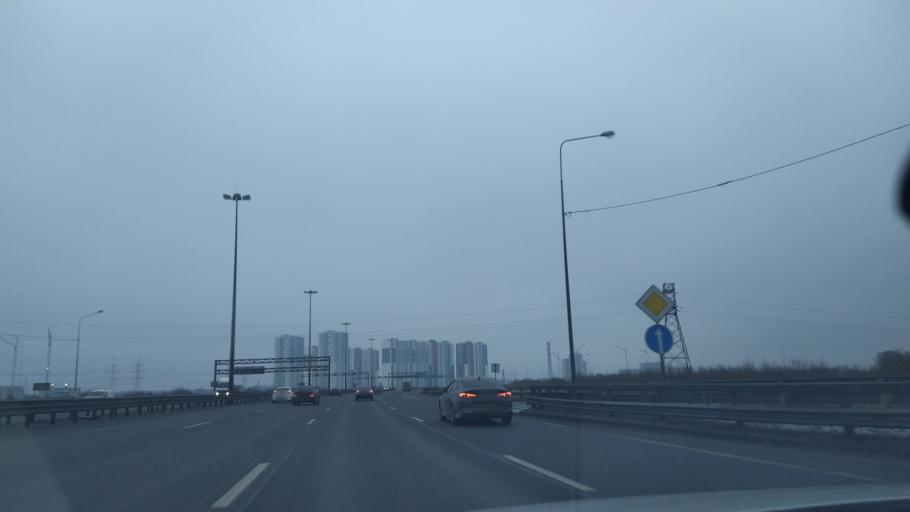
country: RU
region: Leningrad
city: Murino
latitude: 60.0159
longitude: 30.4653
